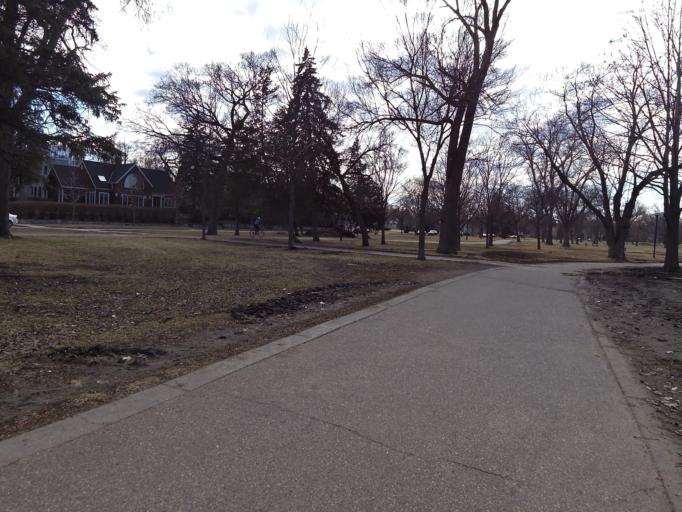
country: US
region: Minnesota
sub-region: Hennepin County
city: Saint Louis Park
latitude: 44.9355
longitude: -93.3163
